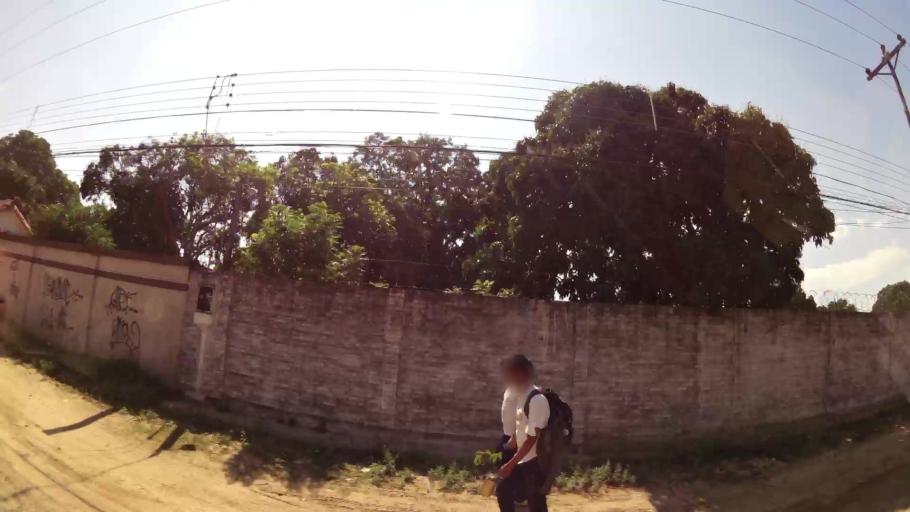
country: BO
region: Santa Cruz
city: Santa Cruz de la Sierra
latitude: -17.7324
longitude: -63.1598
